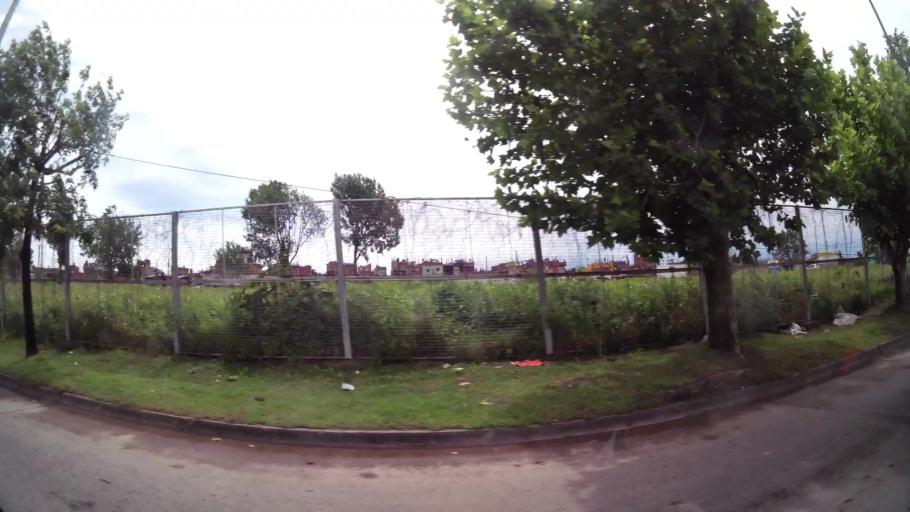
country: AR
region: Buenos Aires F.D.
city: Villa Lugano
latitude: -34.6760
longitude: -58.4625
